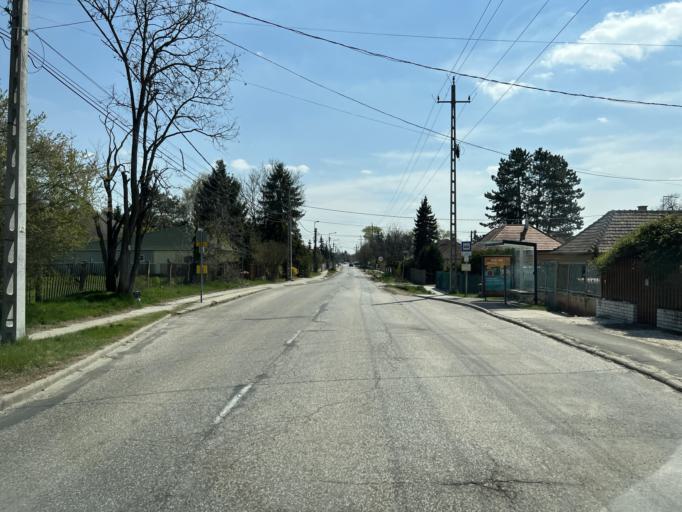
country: HU
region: Pest
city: Szada
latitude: 47.6231
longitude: 19.3403
